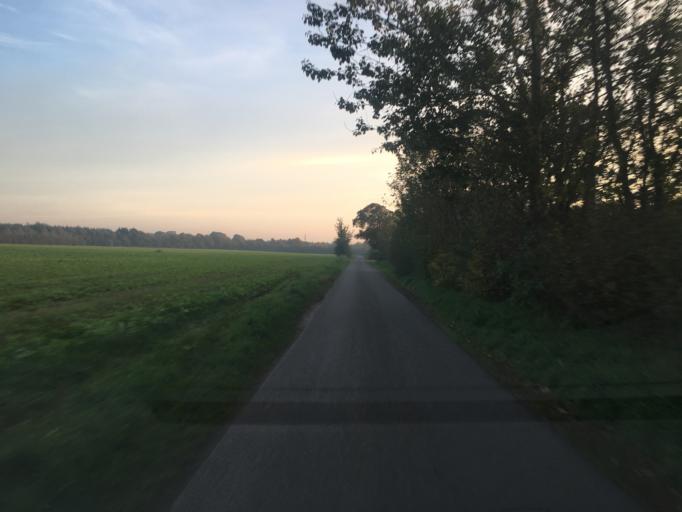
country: DK
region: South Denmark
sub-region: Aabenraa Kommune
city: Tinglev
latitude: 55.0163
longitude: 9.1238
